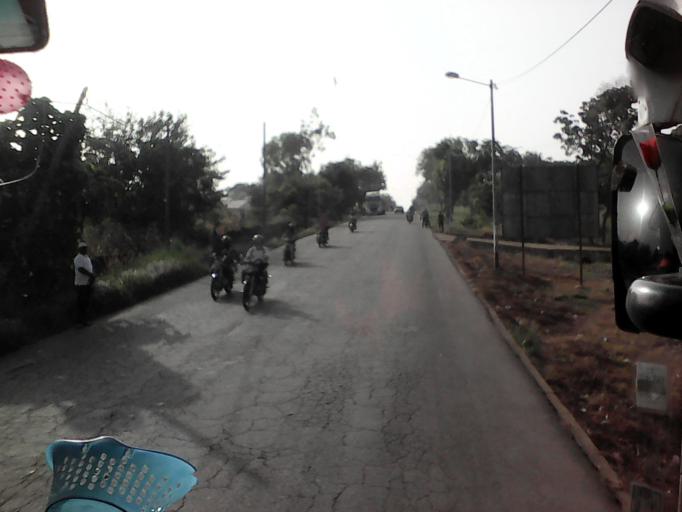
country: TG
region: Kara
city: Kara
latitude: 9.5311
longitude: 1.2020
